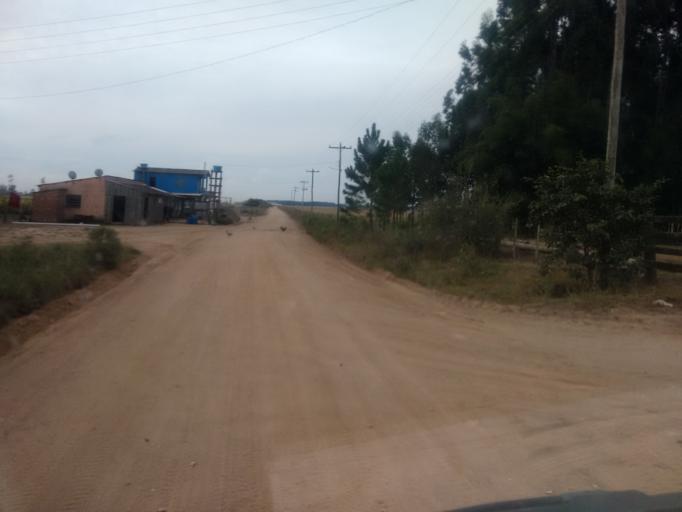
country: BR
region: Rio Grande do Sul
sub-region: Camaqua
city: Camaqua
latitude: -31.1169
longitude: -51.7517
